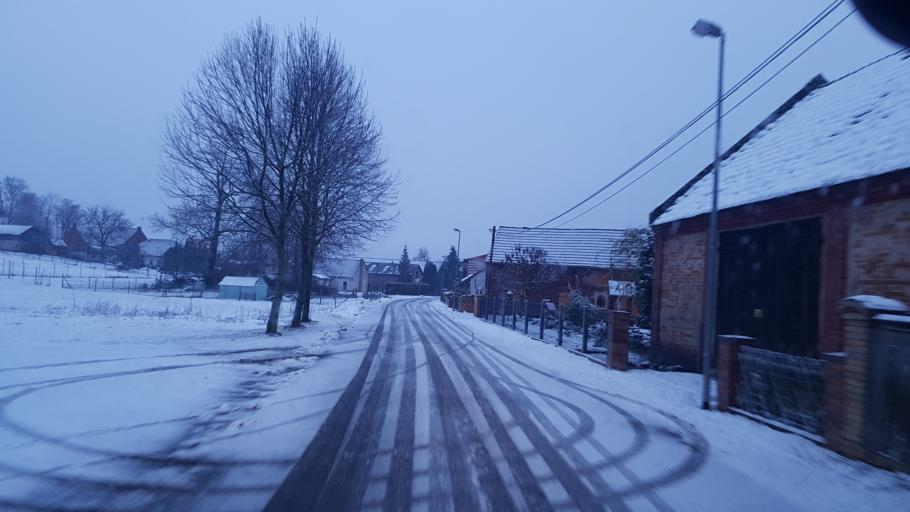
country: DE
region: Brandenburg
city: Tauer
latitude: 51.8974
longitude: 14.4510
